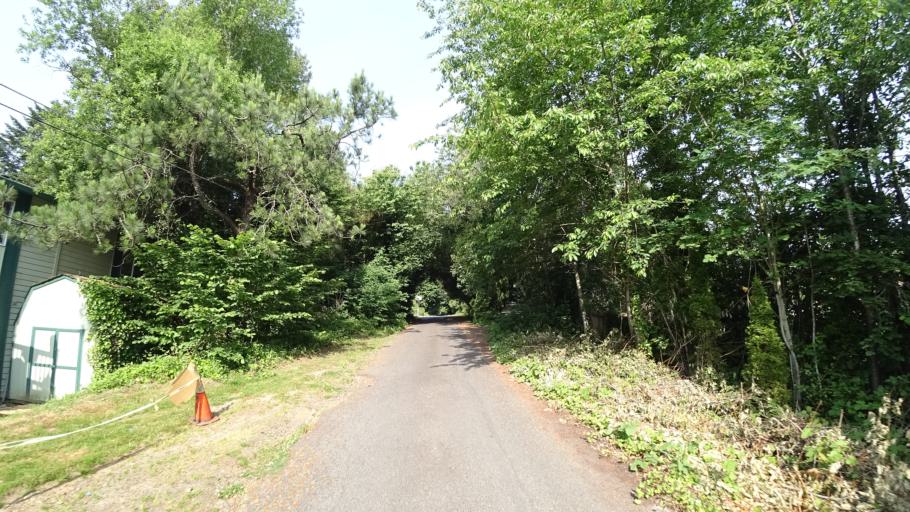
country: US
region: Oregon
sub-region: Washington County
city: Garden Home-Whitford
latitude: 45.4625
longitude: -122.7080
